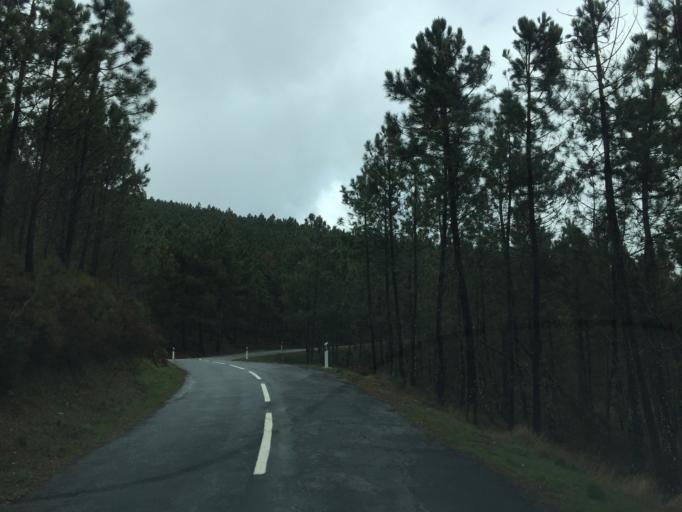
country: PT
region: Guarda
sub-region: Seia
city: Seia
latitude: 40.3345
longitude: -7.7162
